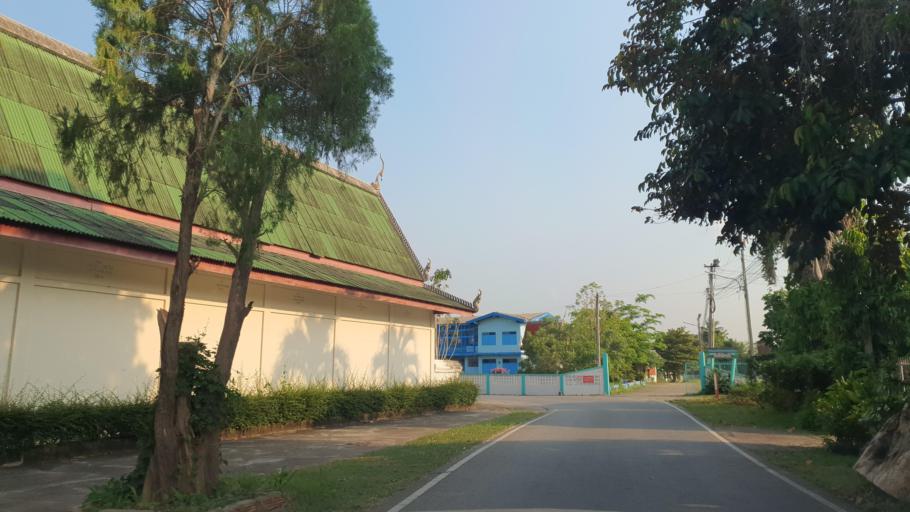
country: TH
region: Chiang Mai
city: San Pa Tong
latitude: 18.6360
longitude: 98.8625
